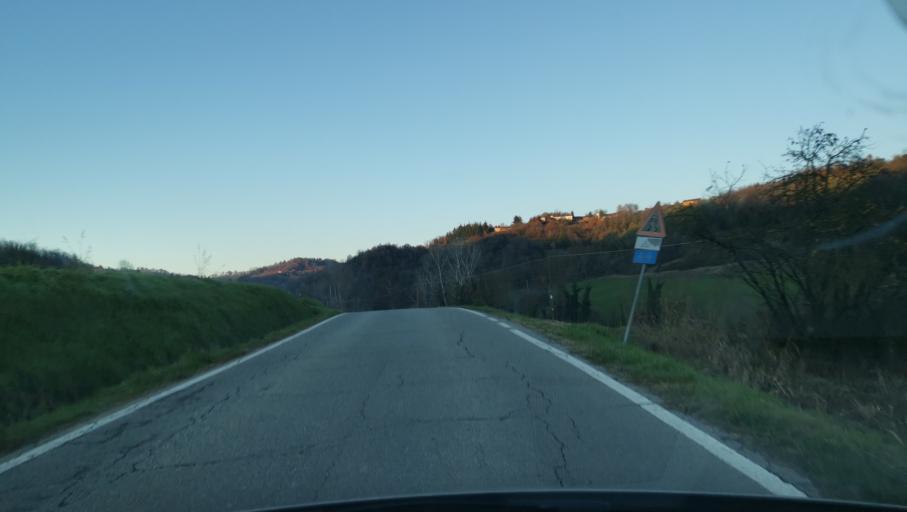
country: IT
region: Piedmont
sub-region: Provincia di Asti
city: Moncucco Torinese
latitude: 45.0703
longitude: 7.9415
